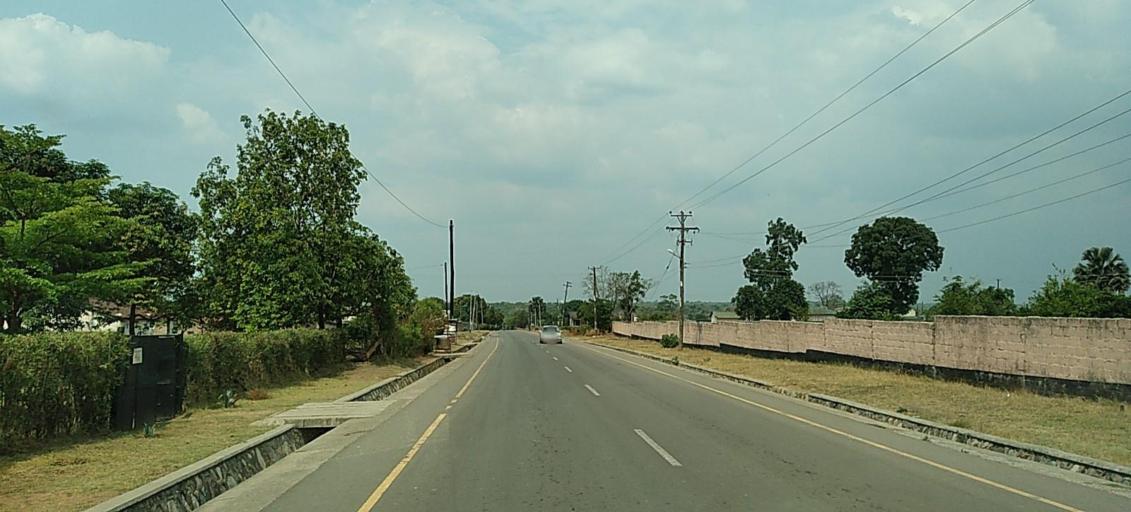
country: ZM
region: Copperbelt
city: Kalulushi
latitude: -12.8511
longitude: 28.1352
